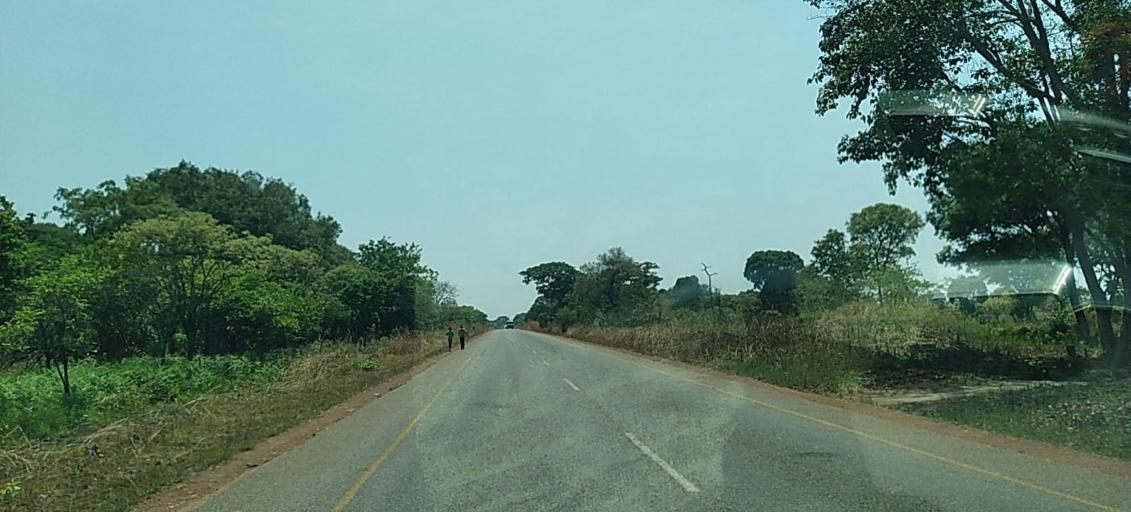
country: ZM
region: North-Western
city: Solwezi
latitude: -12.3848
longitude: 26.1784
